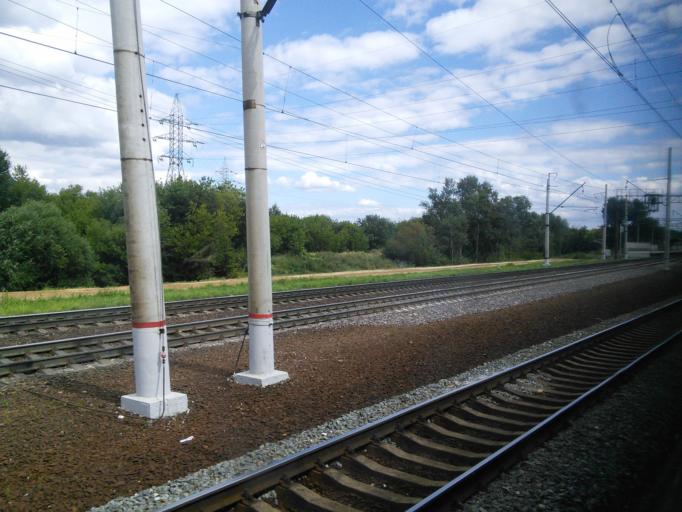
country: RU
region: Moscow
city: Zhulebino
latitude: 55.7073
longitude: 37.8431
